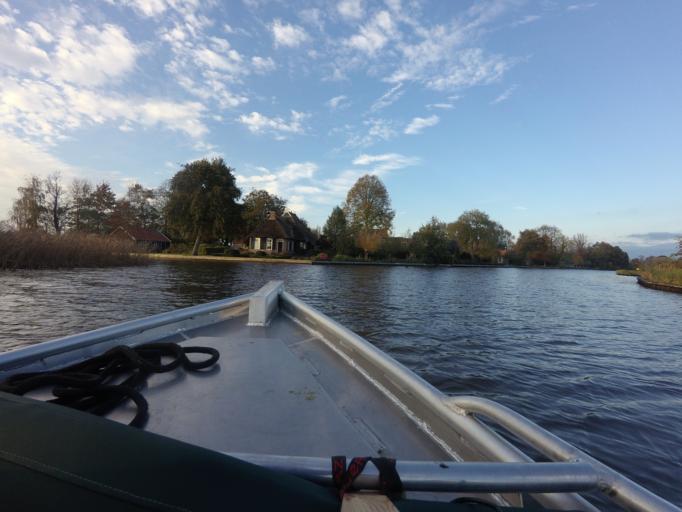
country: NL
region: Overijssel
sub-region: Gemeente Steenwijkerland
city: Blokzijl
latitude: 52.7407
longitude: 5.9931
